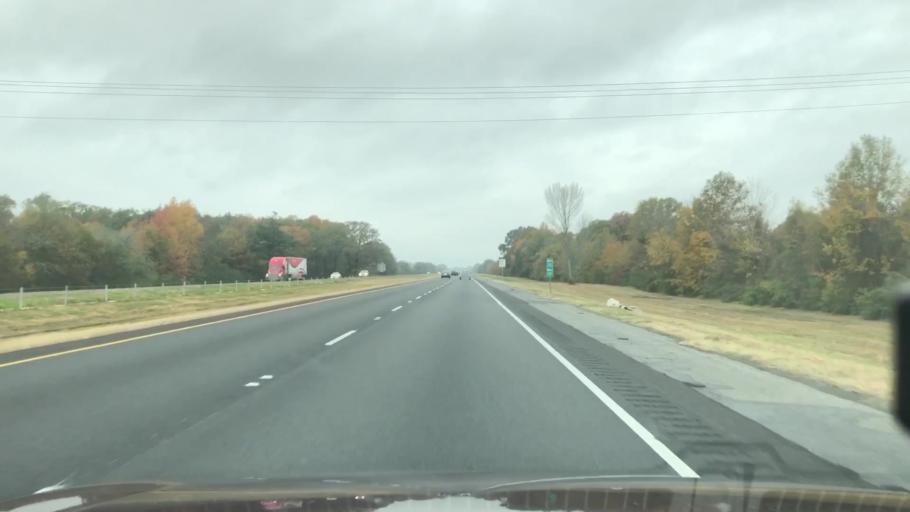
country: US
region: Louisiana
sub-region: Richland Parish
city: Rayville
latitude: 32.4594
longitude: -91.7751
